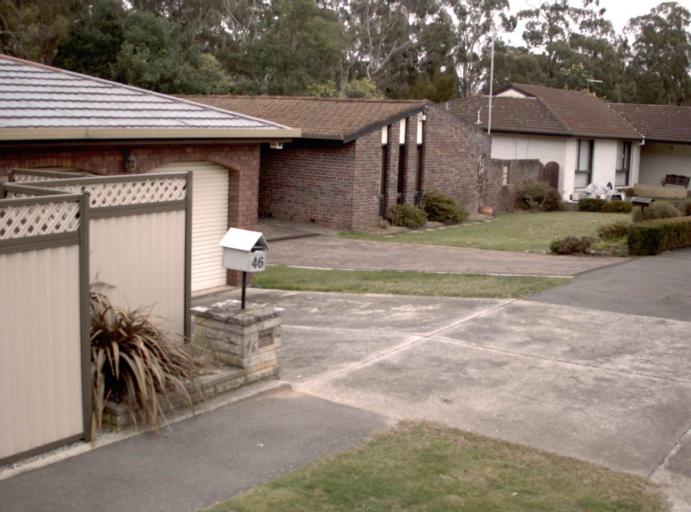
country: AU
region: Tasmania
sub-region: Launceston
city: Newstead
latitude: -41.4639
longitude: 147.1725
